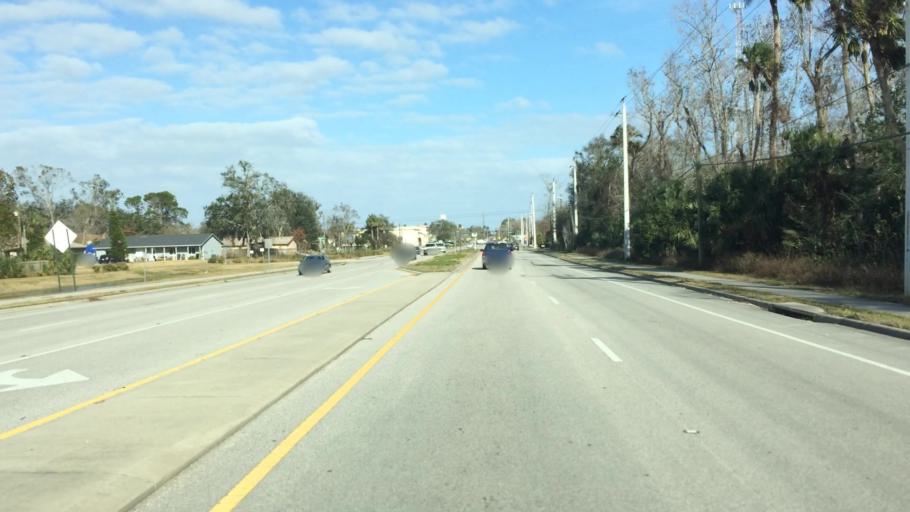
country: US
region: Florida
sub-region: Volusia County
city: Holly Hill
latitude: 29.2373
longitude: -81.0620
